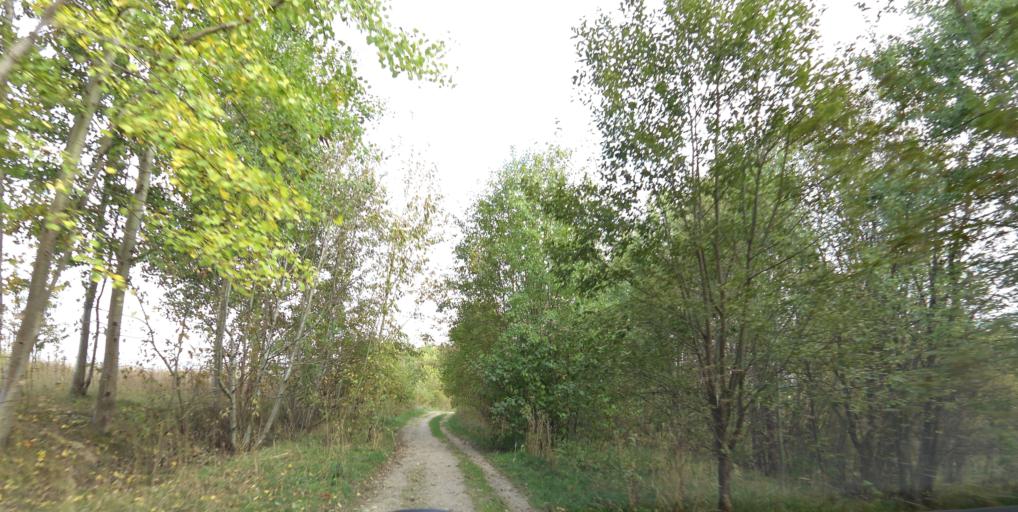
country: LT
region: Vilnius County
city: Justiniskes
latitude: 54.7153
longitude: 25.2095
